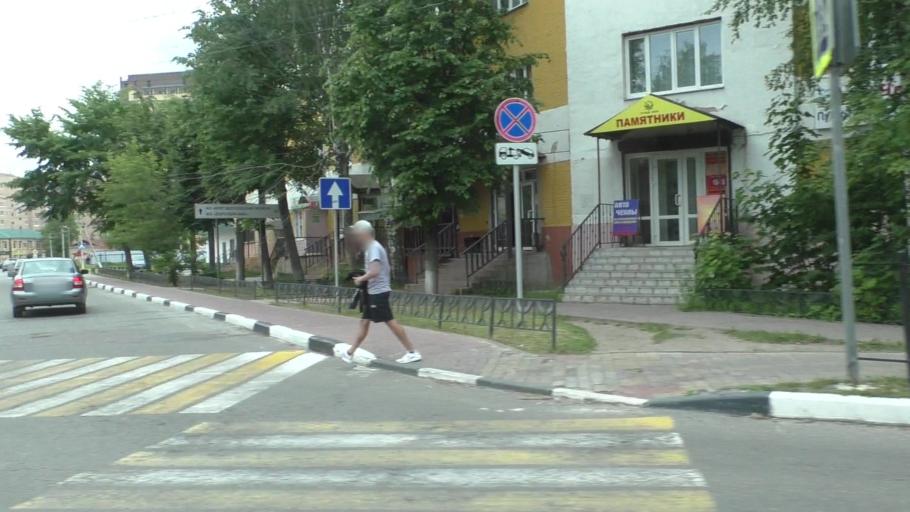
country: RU
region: Moskovskaya
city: Yegor'yevsk
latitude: 55.3752
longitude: 39.0479
